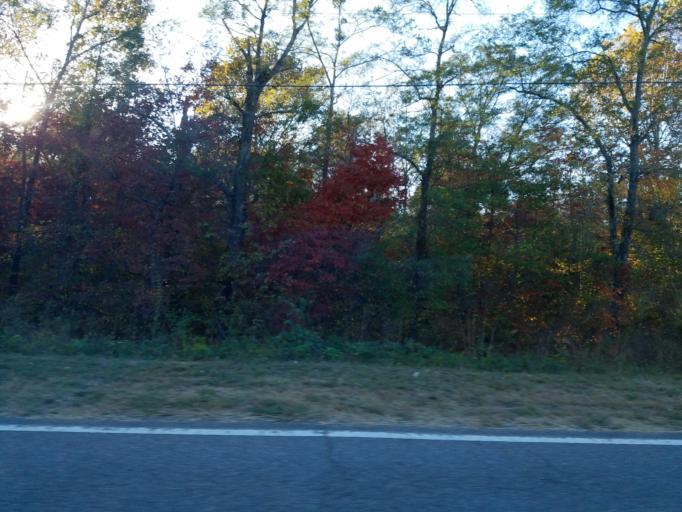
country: US
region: Georgia
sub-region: Bartow County
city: Euharlee
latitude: 34.2486
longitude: -84.9595
